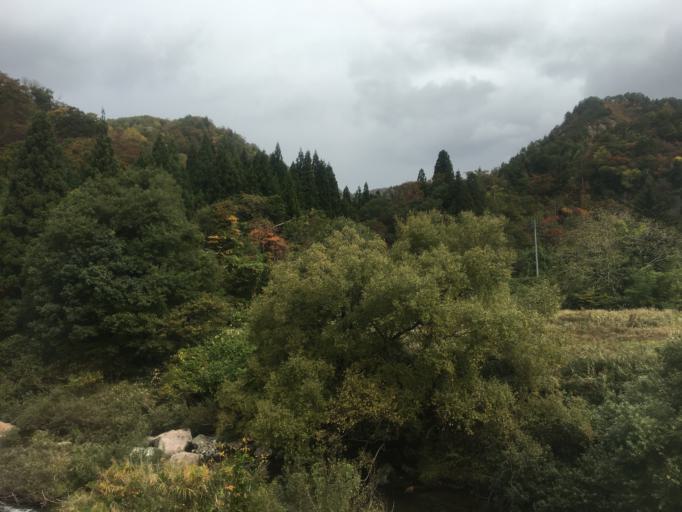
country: JP
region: Yamagata
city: Nagai
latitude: 38.0539
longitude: 139.7940
